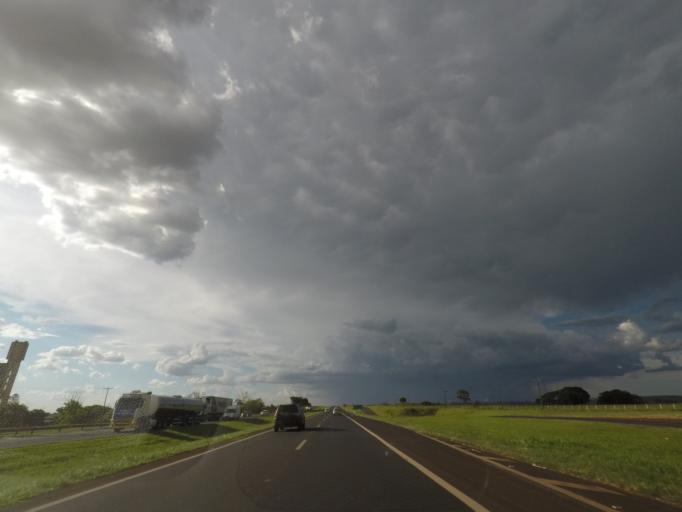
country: BR
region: Sao Paulo
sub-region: Jardinopolis
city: Jardinopolis
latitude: -21.0850
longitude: -47.8000
